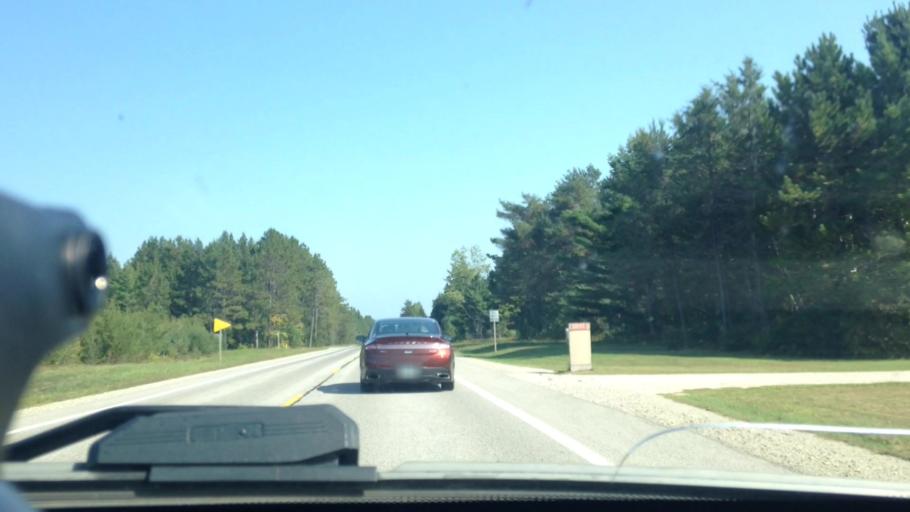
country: US
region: Michigan
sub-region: Luce County
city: Newberry
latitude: 46.3036
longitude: -85.4491
